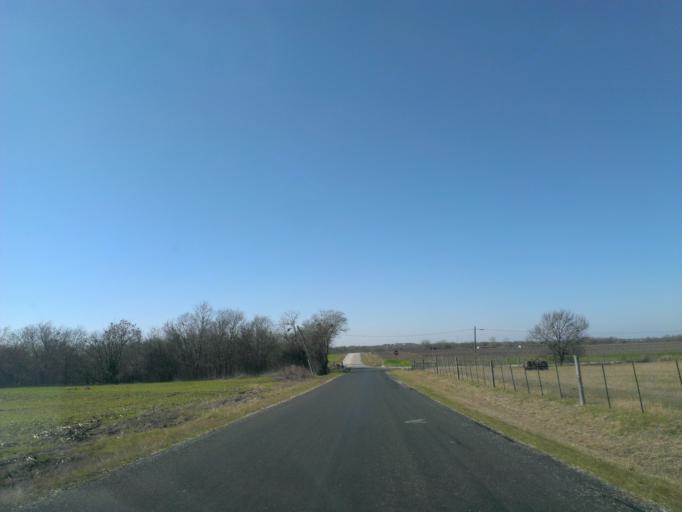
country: US
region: Texas
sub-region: Williamson County
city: Georgetown
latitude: 30.6520
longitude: -97.5770
